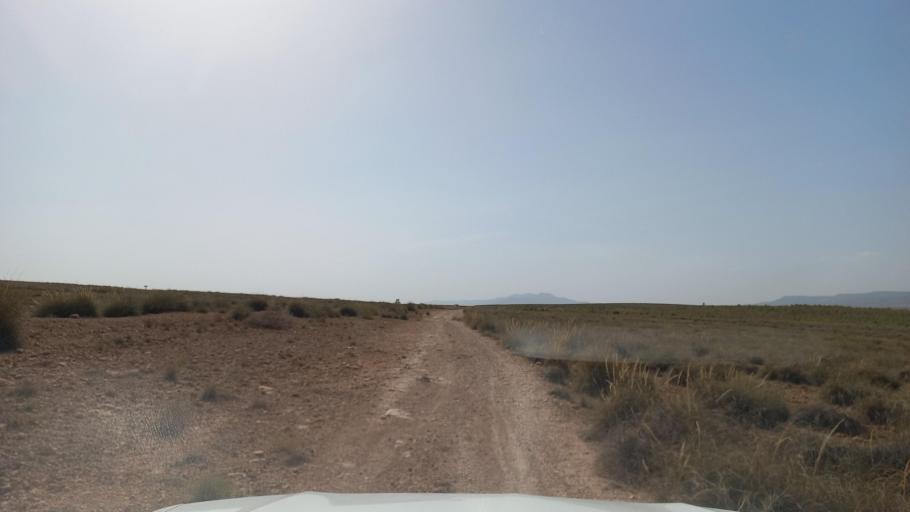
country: TN
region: Al Qasrayn
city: Kasserine
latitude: 35.2154
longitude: 8.9859
